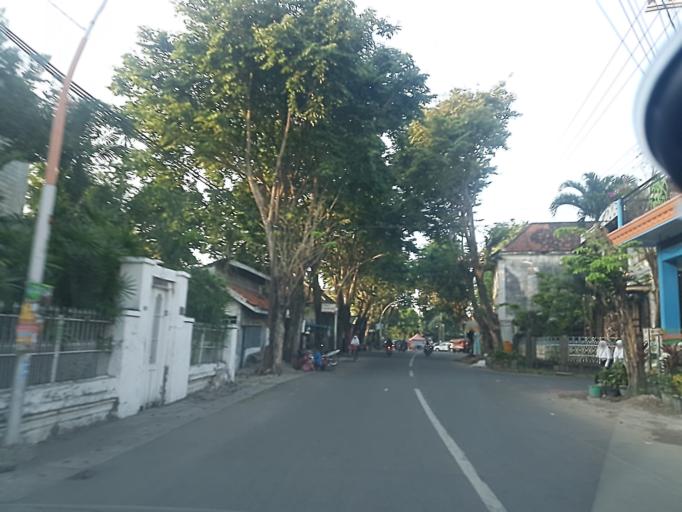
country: ID
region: East Java
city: Gresik
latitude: -7.1539
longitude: 112.6582
